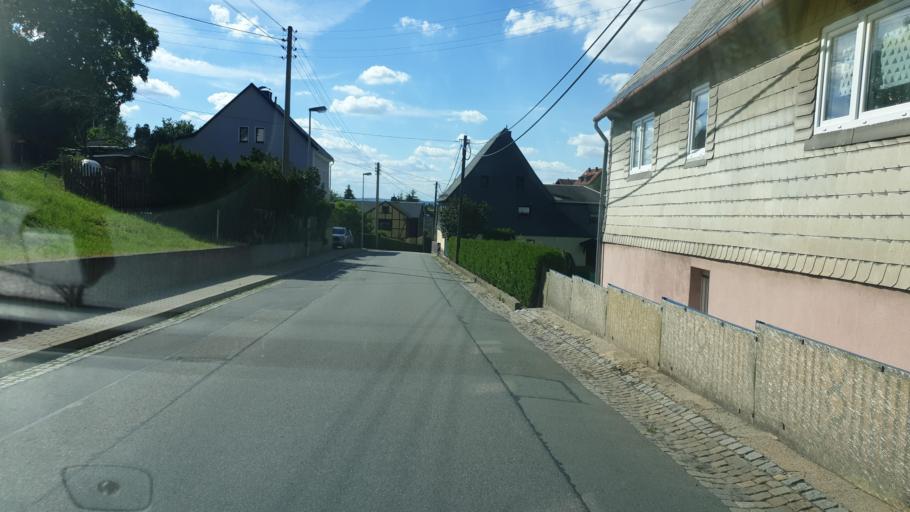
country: DE
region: Saxony
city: Burkhardtsdorf
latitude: 50.7548
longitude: 12.9223
